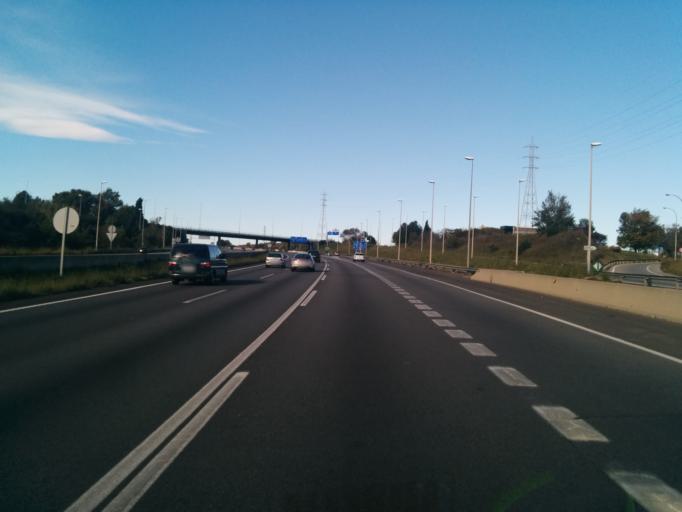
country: ES
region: Catalonia
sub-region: Provincia de Barcelona
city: Cerdanyola del Valles
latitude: 41.5042
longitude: 2.1404
